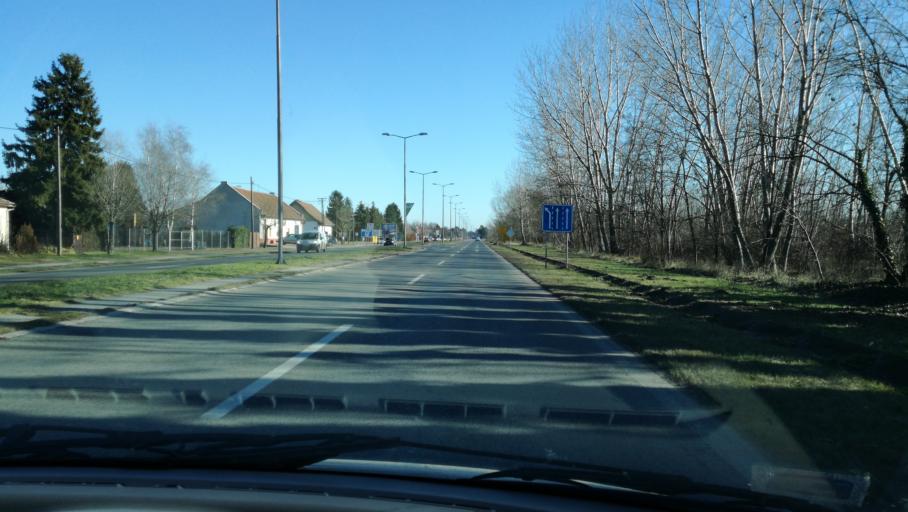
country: RS
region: Autonomna Pokrajina Vojvodina
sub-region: Severnobacki Okrug
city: Subotica
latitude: 46.1045
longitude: 19.7333
